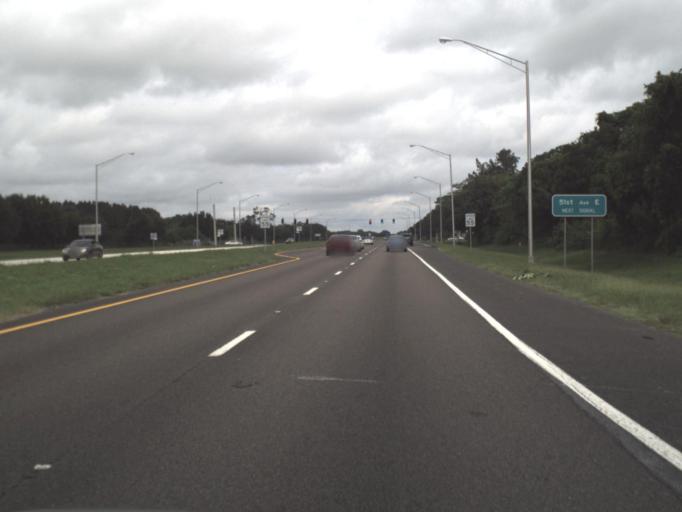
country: US
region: Florida
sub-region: Manatee County
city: Samoset
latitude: 27.4483
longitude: -82.5302
